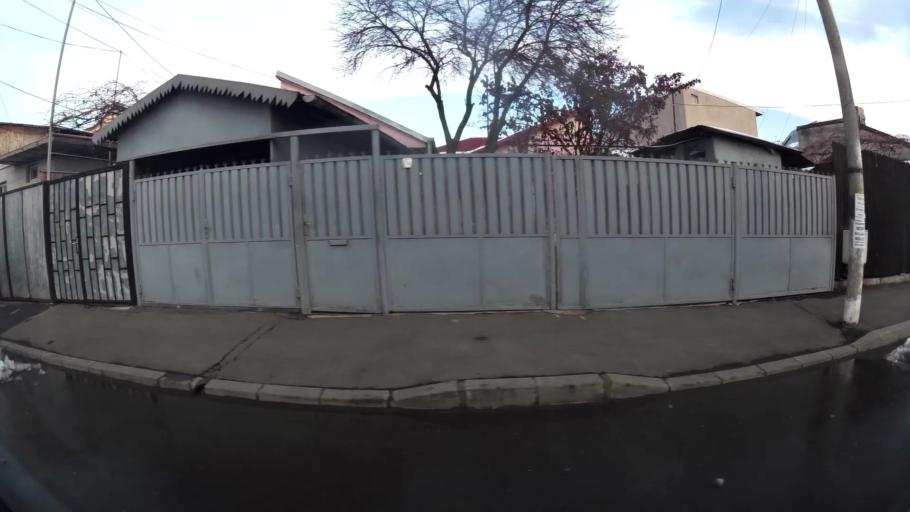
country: RO
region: Bucuresti
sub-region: Municipiul Bucuresti
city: Bucuresti
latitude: 44.3949
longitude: 26.0775
